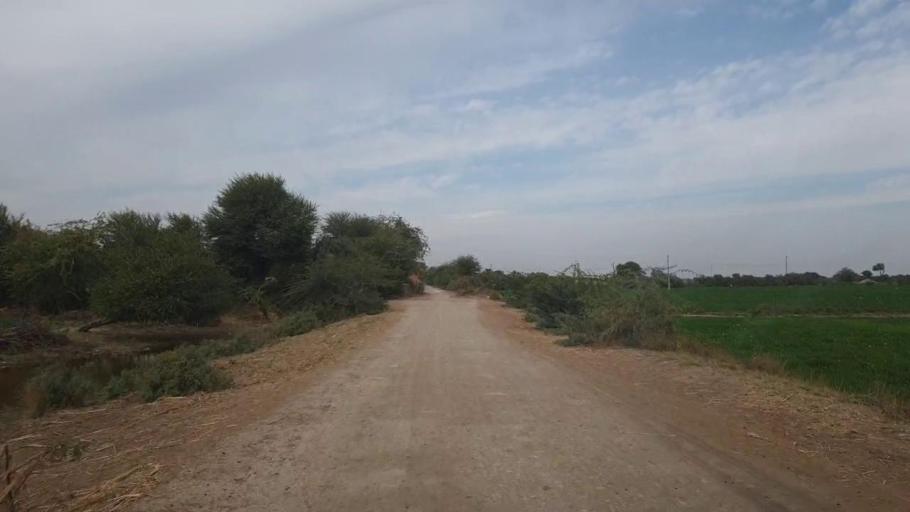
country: PK
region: Sindh
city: Sanghar
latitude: 26.0417
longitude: 68.9064
